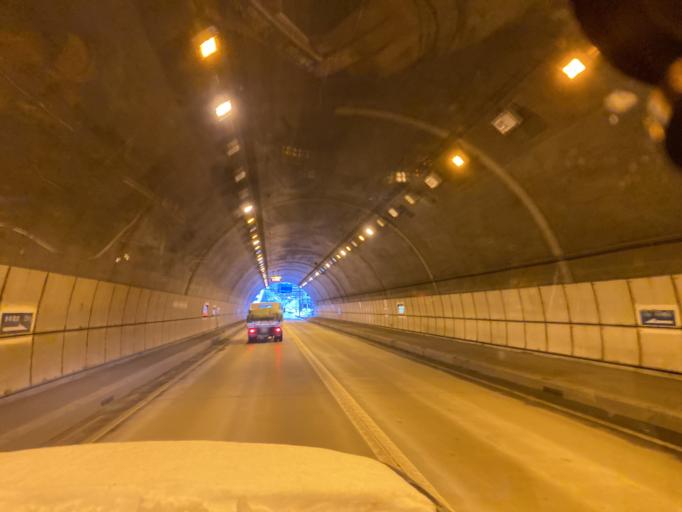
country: JP
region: Nagano
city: Nagano-shi
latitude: 36.6183
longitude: 138.1255
